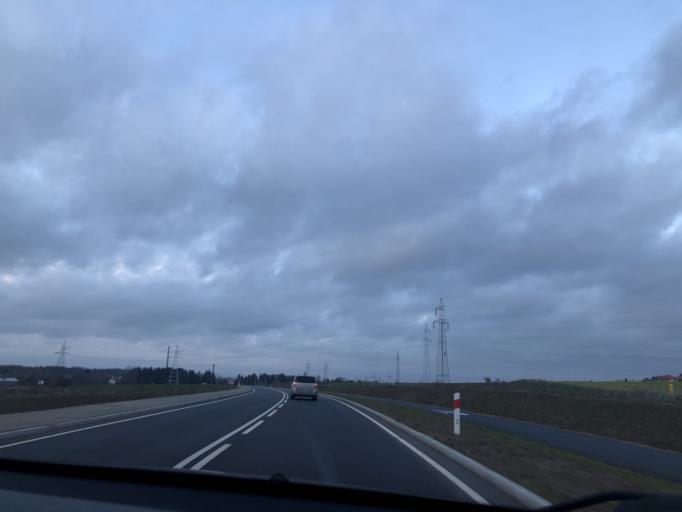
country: PL
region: Podlasie
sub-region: Lomza
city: Lomza
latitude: 53.1467
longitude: 22.0528
